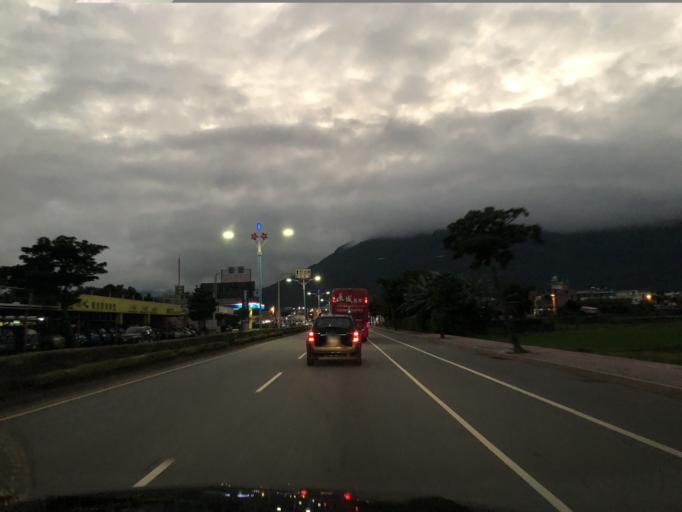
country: TW
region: Taiwan
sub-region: Hualien
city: Hualian
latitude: 23.9762
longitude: 121.5778
